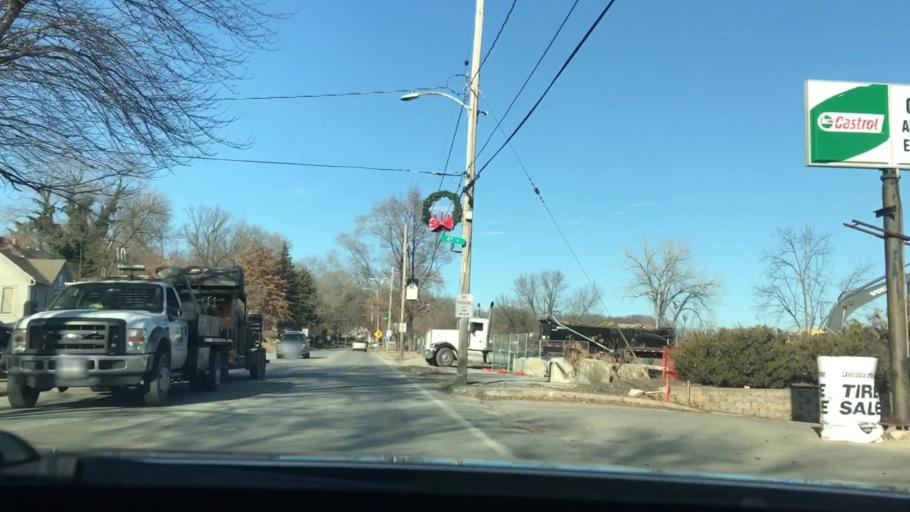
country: US
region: Missouri
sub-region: Platte County
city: Parkville
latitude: 39.1907
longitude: -94.6829
